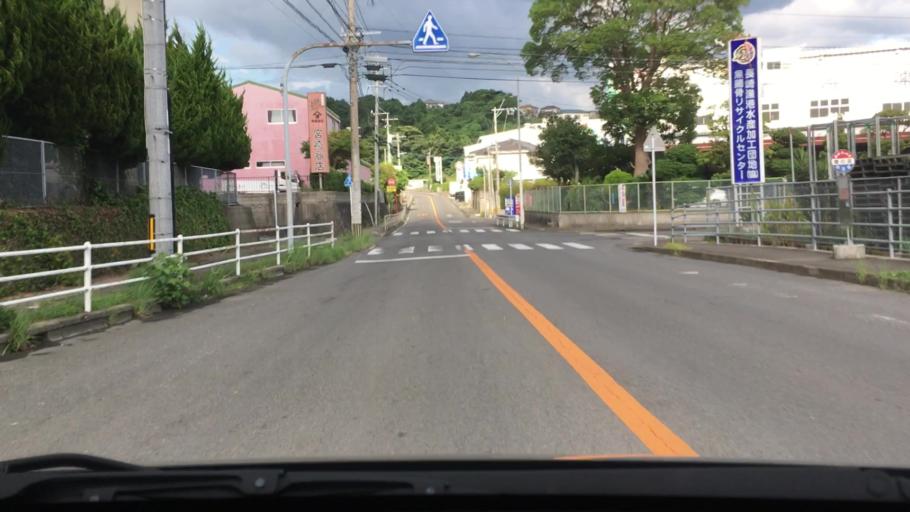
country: JP
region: Nagasaki
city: Togitsu
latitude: 32.8259
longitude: 129.7652
